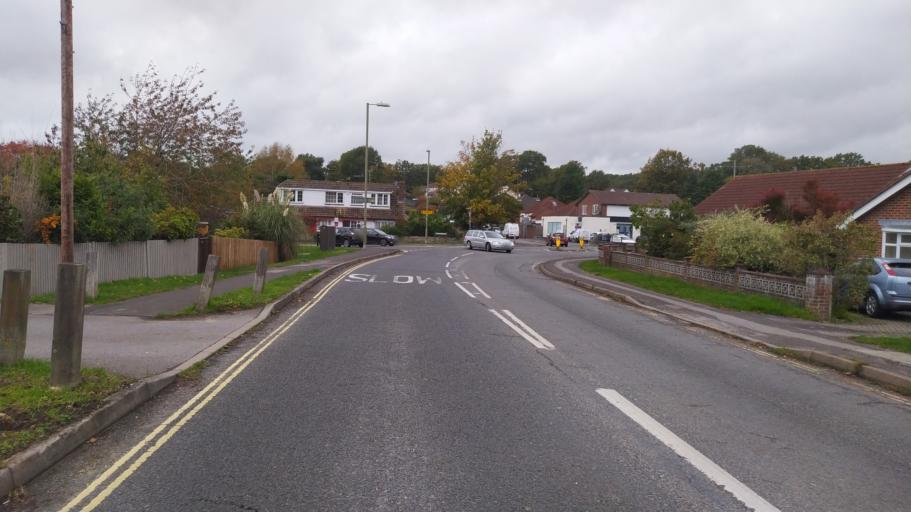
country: GB
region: England
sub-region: Hampshire
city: Cowplain
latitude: 50.9042
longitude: -1.0208
